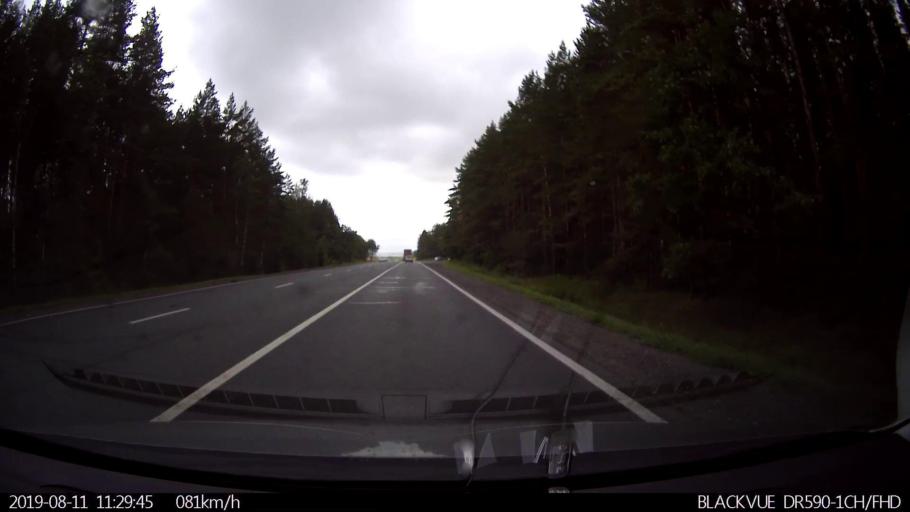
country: RU
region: Ulyanovsk
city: Krasnyy Gulyay
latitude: 54.0664
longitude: 48.2220
